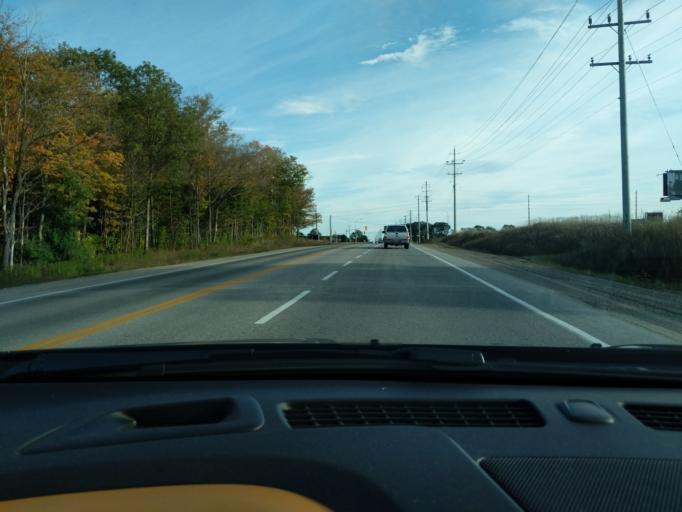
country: CA
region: Ontario
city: Barrie
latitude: 44.4015
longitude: -79.7423
